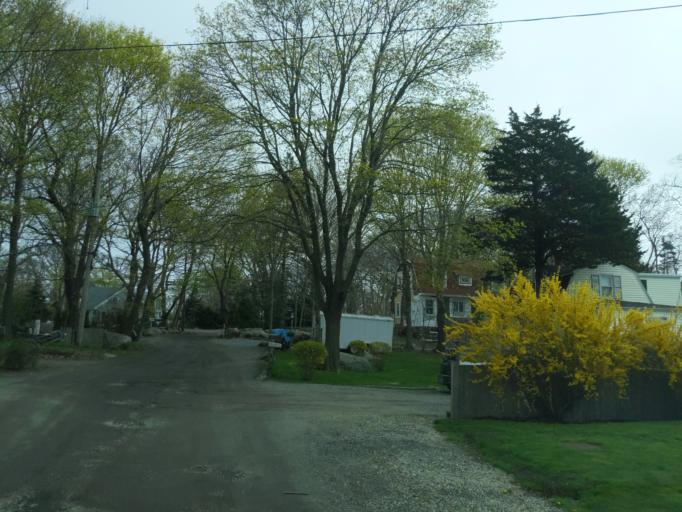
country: US
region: Massachusetts
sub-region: Essex County
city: Rockport
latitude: 42.6529
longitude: -70.6028
